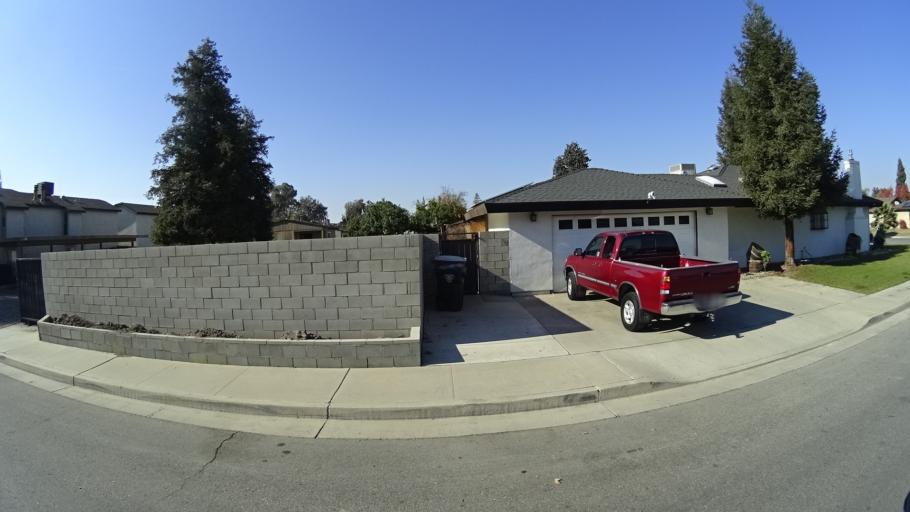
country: US
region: California
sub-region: Kern County
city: Greenfield
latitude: 35.2978
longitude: -119.0528
